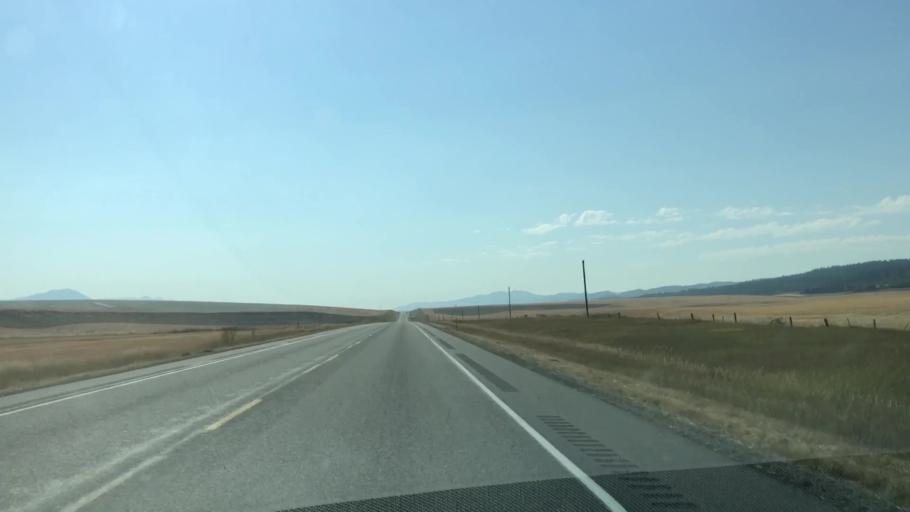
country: US
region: Idaho
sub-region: Madison County
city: Rexburg
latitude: 43.5393
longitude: -111.5164
